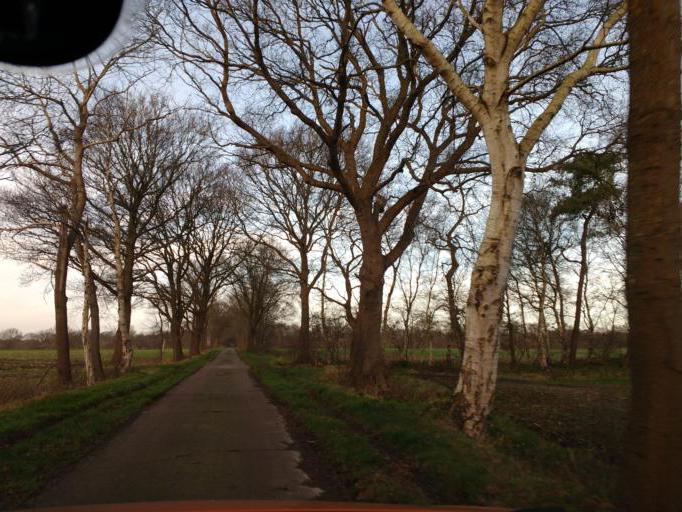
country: DE
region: Lower Saxony
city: Hatten
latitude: 53.1207
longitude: 8.3847
